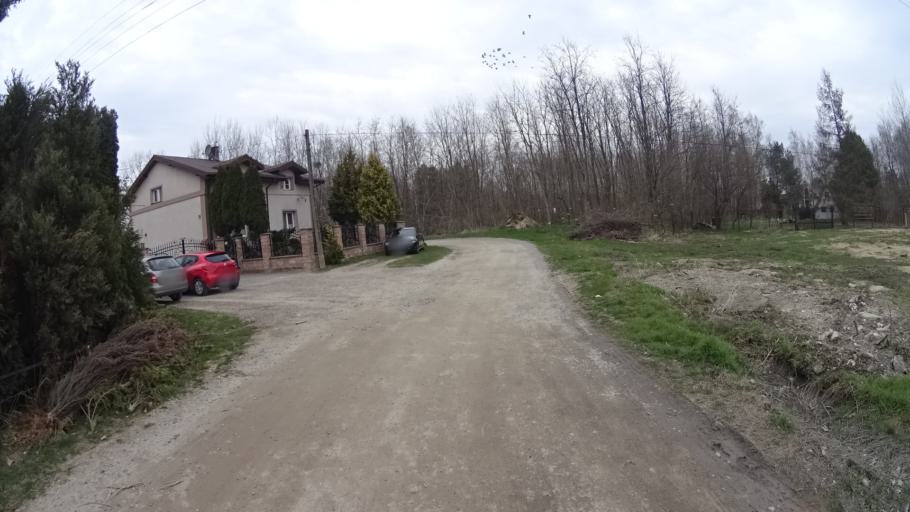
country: PL
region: Masovian Voivodeship
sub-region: Powiat warszawski zachodni
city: Jozefow
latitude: 52.2453
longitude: 20.6885
